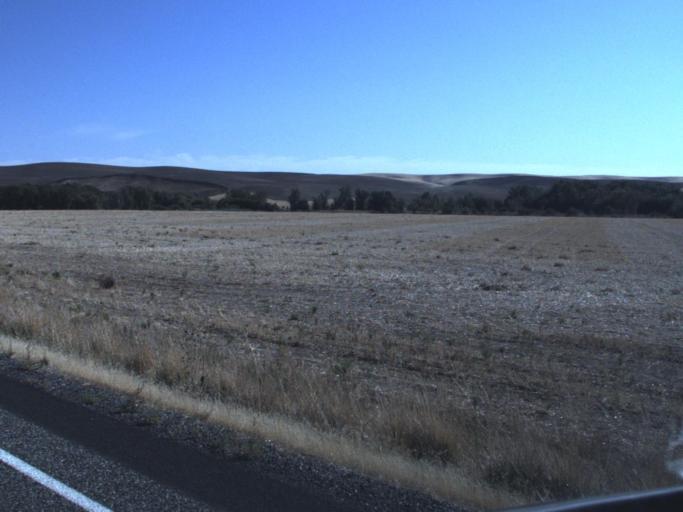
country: US
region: Washington
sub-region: Walla Walla County
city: Walla Walla
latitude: 46.2992
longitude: -118.3959
